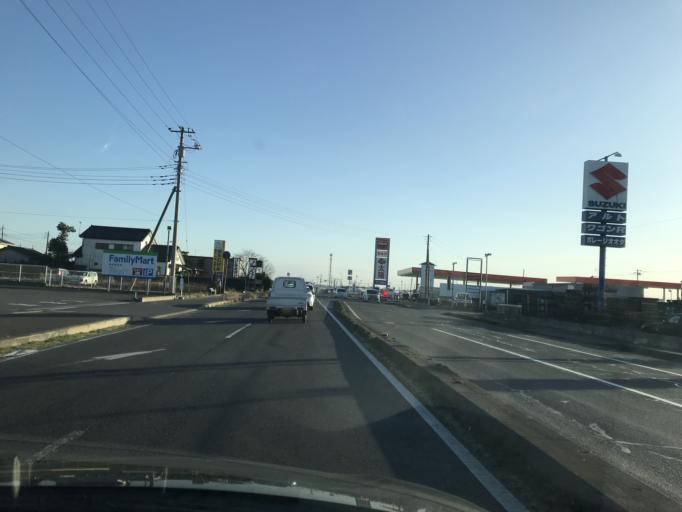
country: JP
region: Chiba
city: Omigawa
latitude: 35.8824
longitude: 140.6311
